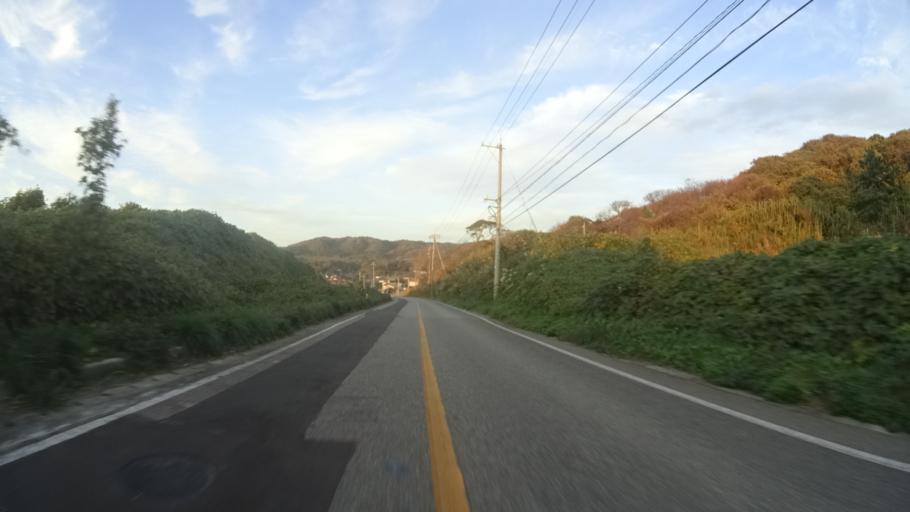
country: JP
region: Ishikawa
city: Nanao
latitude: 37.2253
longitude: 136.7041
